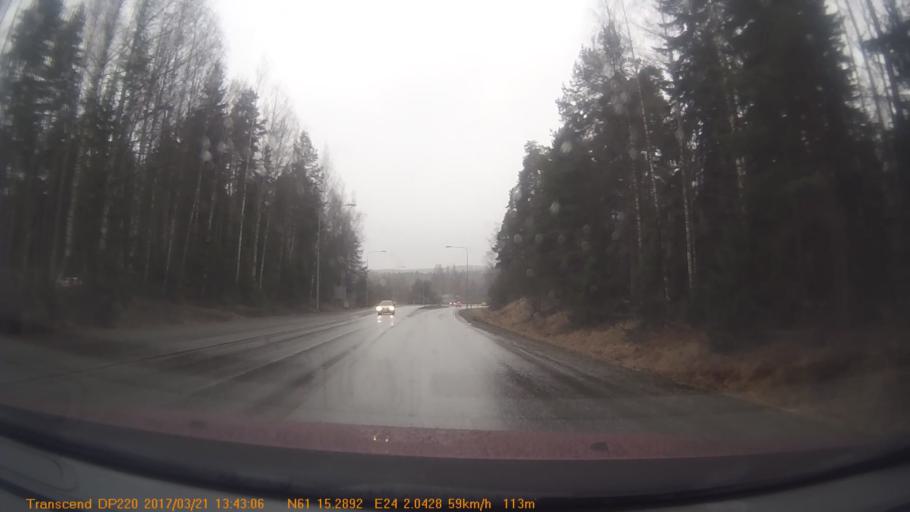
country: FI
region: Pirkanmaa
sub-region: Etelae-Pirkanmaa
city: Valkeakoski
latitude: 61.2550
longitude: 24.0341
